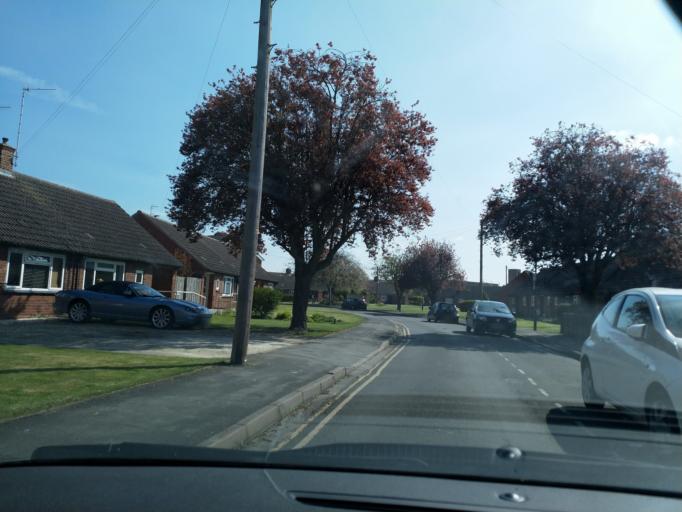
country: GB
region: England
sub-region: Warwickshire
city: Stratford-upon-Avon
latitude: 52.1963
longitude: -1.7227
